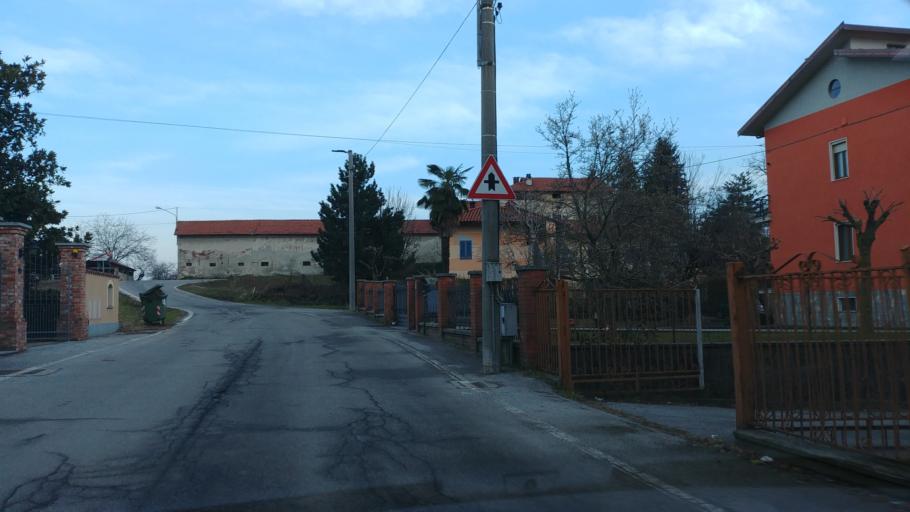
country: IT
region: Piedmont
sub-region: Provincia di Cuneo
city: Cuneo
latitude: 44.3978
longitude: 7.5780
